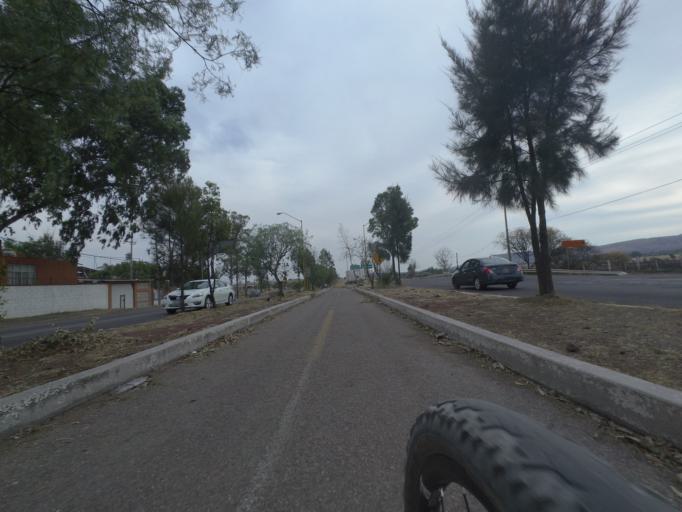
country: MX
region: Aguascalientes
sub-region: Aguascalientes
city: La Loma de los Negritos
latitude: 21.8660
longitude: -102.3716
